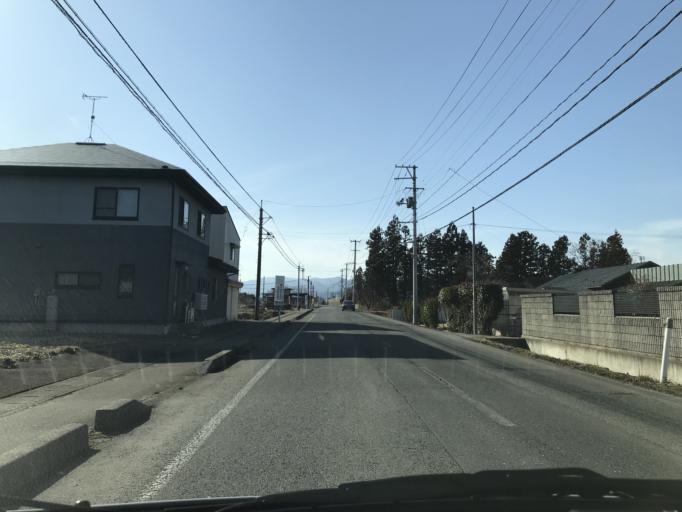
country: JP
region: Iwate
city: Kitakami
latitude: 39.3024
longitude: 141.0266
